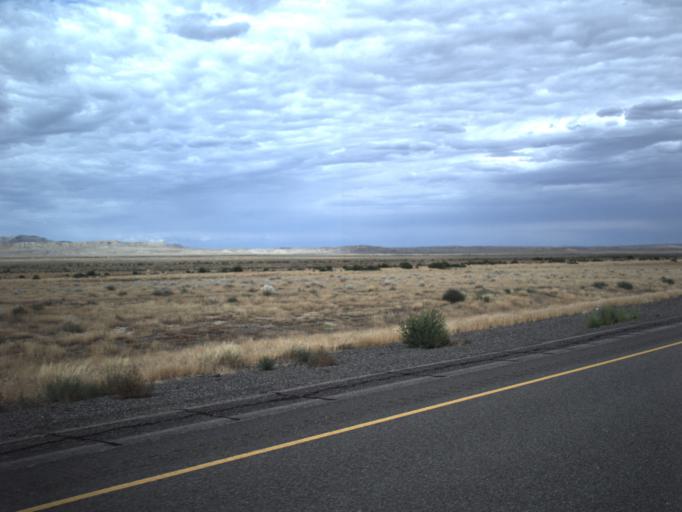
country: US
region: Utah
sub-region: Grand County
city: Moab
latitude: 38.9418
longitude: -109.6015
